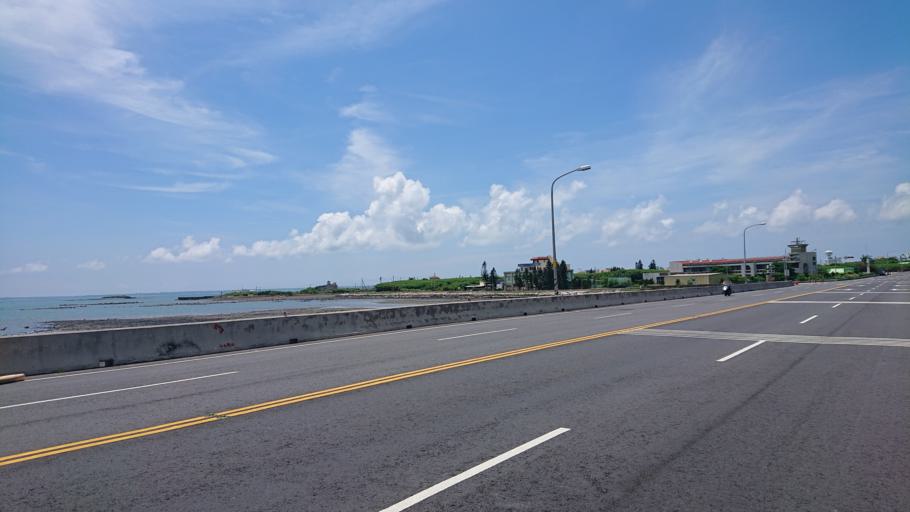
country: TW
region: Taiwan
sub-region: Penghu
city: Ma-kung
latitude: 23.6094
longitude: 119.6106
